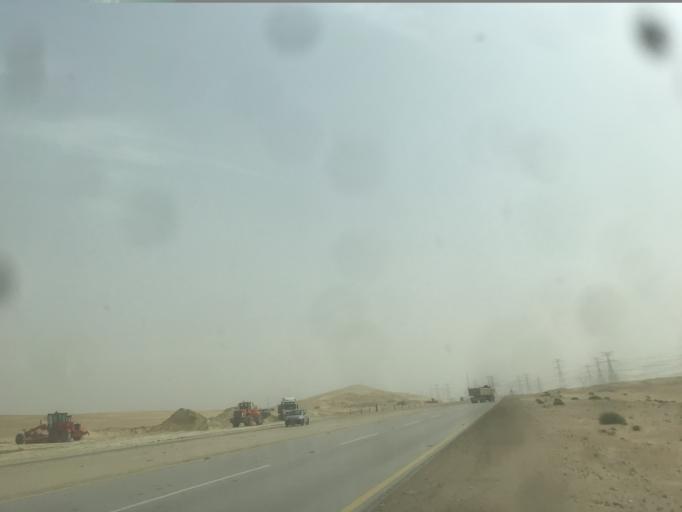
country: SA
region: Eastern Province
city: Abqaiq
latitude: 25.9098
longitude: 49.8839
